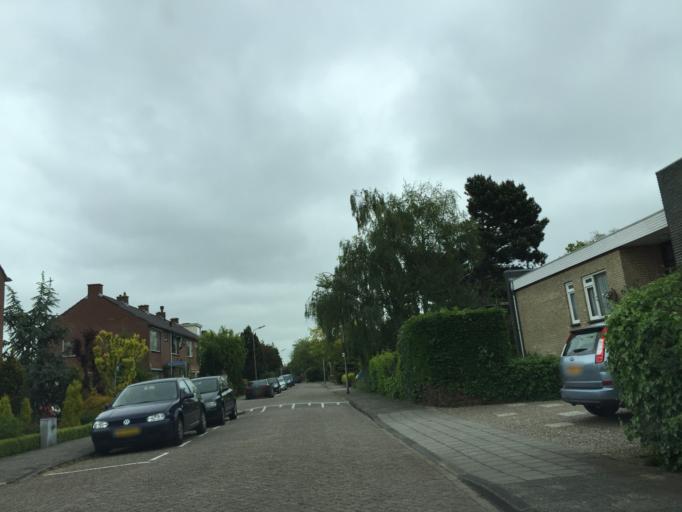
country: NL
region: South Holland
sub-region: Gemeente Den Haag
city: Ypenburg
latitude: 52.0407
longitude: 4.3884
